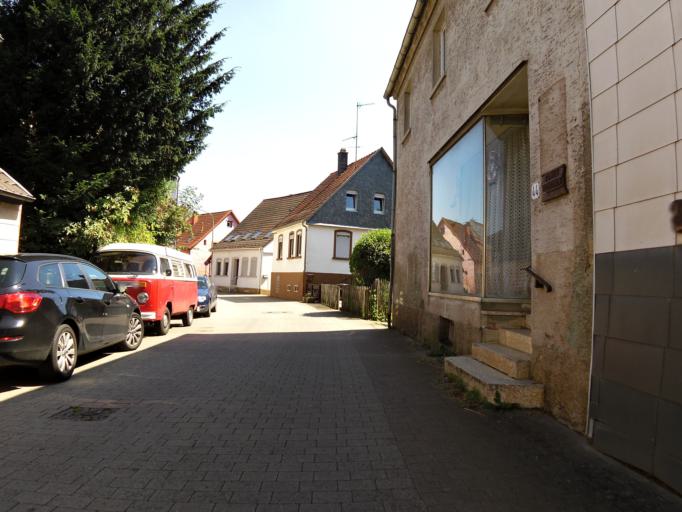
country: DE
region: Rheinland-Pfalz
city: Imsbach
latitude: 49.5823
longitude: 7.8808
